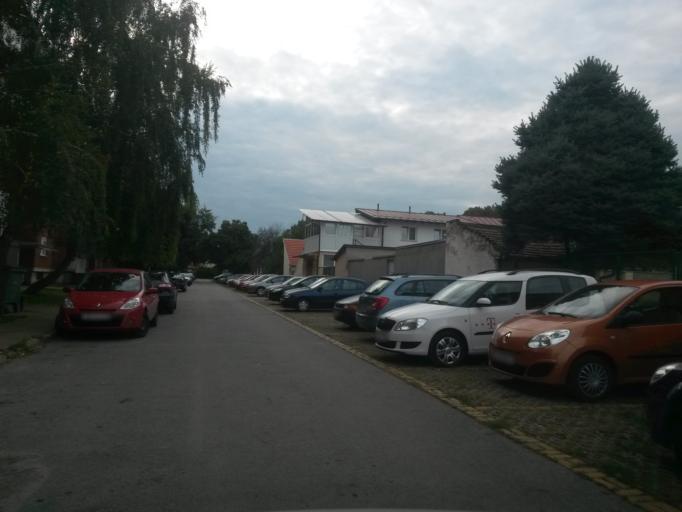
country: HR
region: Osjecko-Baranjska
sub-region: Grad Osijek
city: Osijek
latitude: 45.5509
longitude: 18.6859
